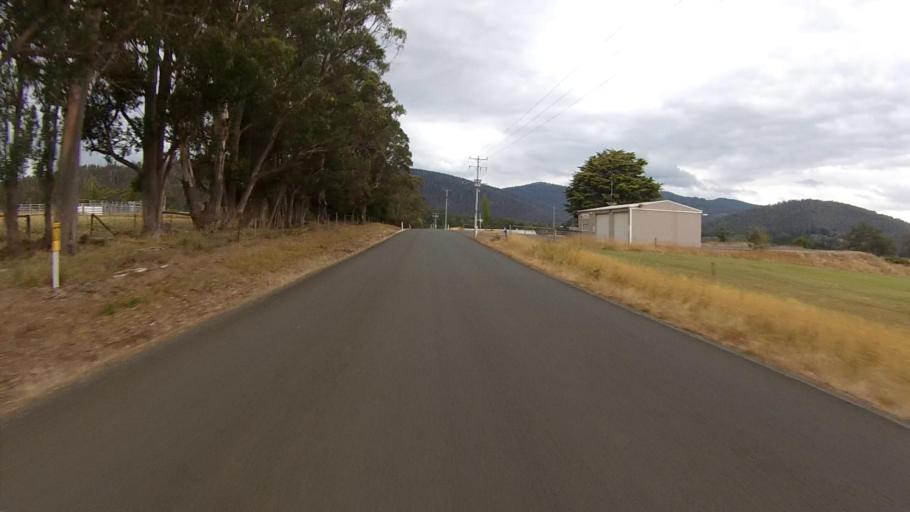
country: AU
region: Tasmania
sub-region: Huon Valley
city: Huonville
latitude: -42.9759
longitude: 147.0940
